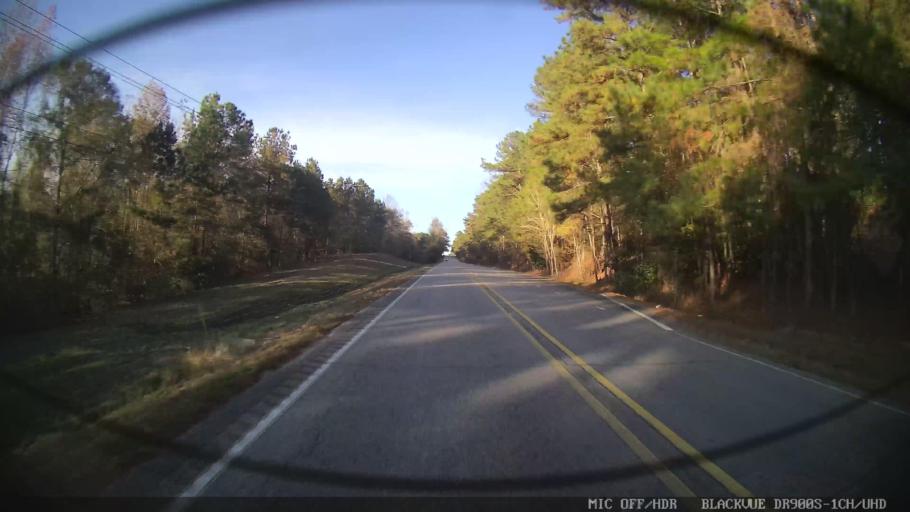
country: US
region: Mississippi
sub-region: Lamar County
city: Purvis
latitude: 31.0924
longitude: -89.4151
